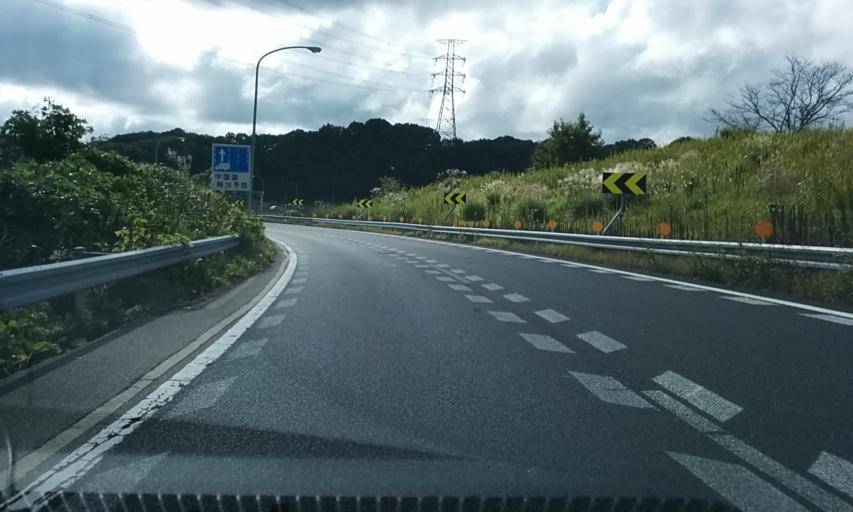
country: JP
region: Hyogo
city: Sandacho
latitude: 34.8946
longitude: 135.1519
